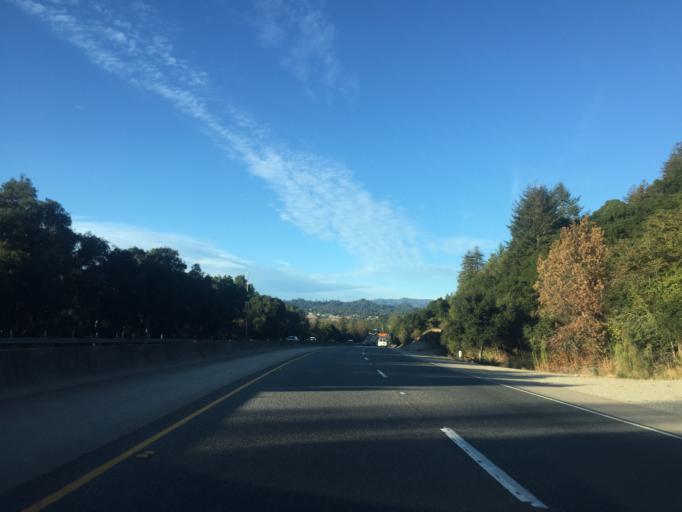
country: US
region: California
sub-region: Santa Cruz County
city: Scotts Valley
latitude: 37.0447
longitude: -122.0152
